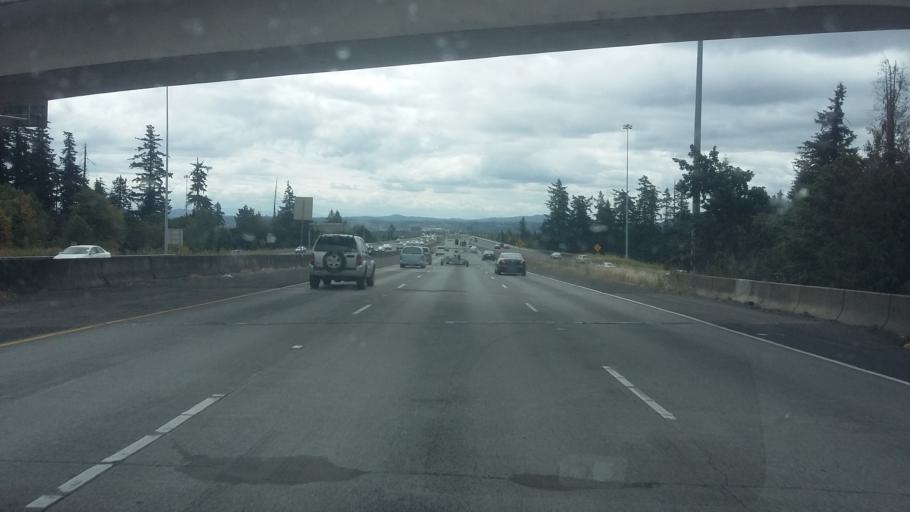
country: US
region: Washington
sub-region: Clark County
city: Orchards
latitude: 45.6067
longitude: -122.5521
